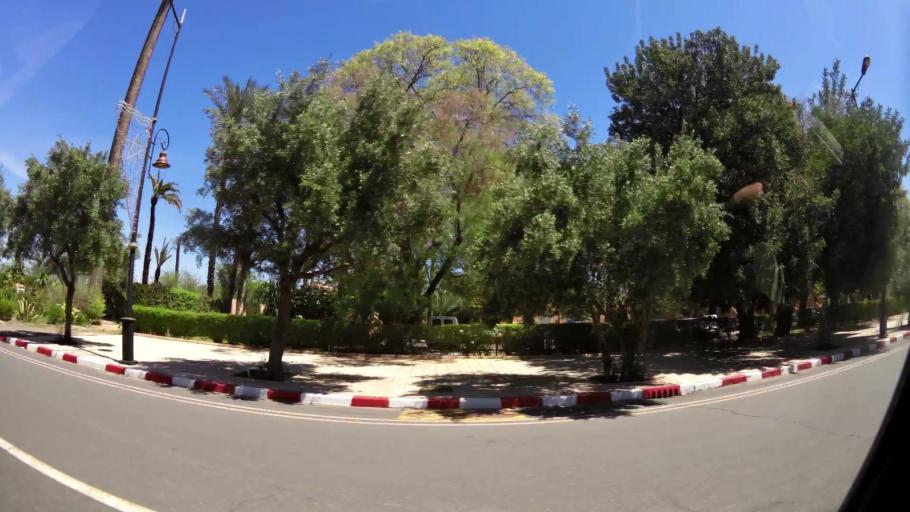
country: MA
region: Marrakech-Tensift-Al Haouz
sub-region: Marrakech
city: Marrakesh
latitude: 31.6240
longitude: -8.0086
